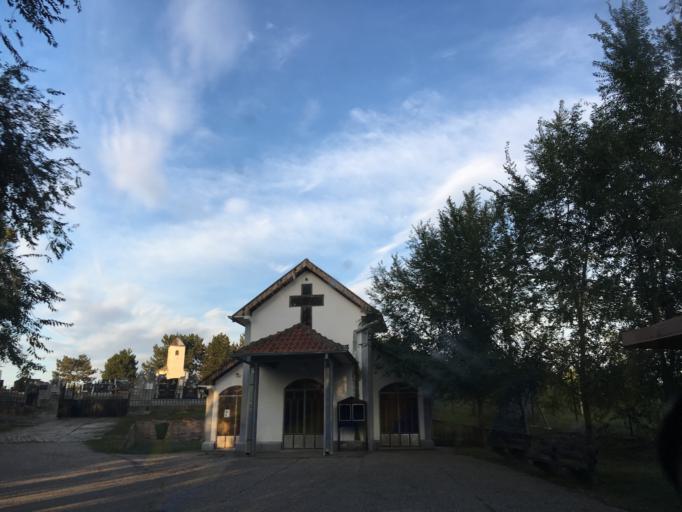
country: RS
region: Autonomna Pokrajina Vojvodina
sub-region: Juznobanatski Okrug
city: Kovin
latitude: 44.8822
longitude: 20.9757
